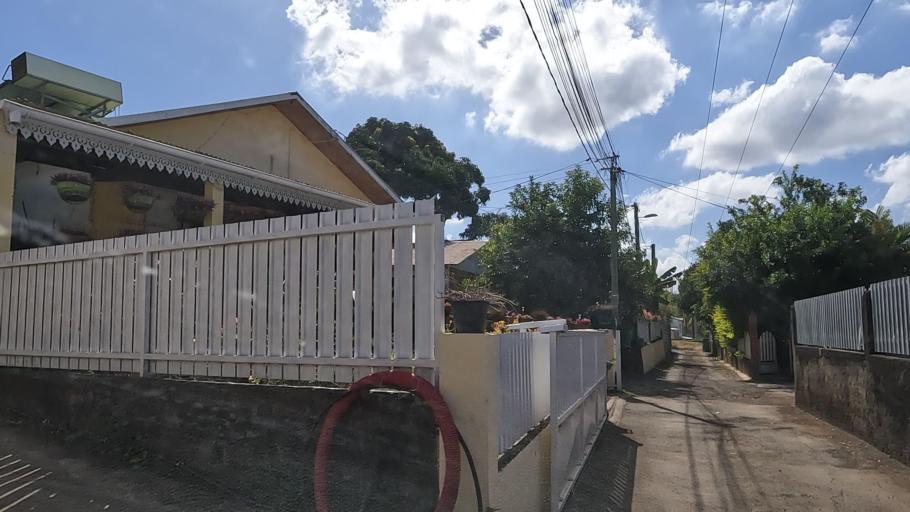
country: RE
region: Reunion
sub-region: Reunion
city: L'Entre-Deux
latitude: -21.2522
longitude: 55.4344
